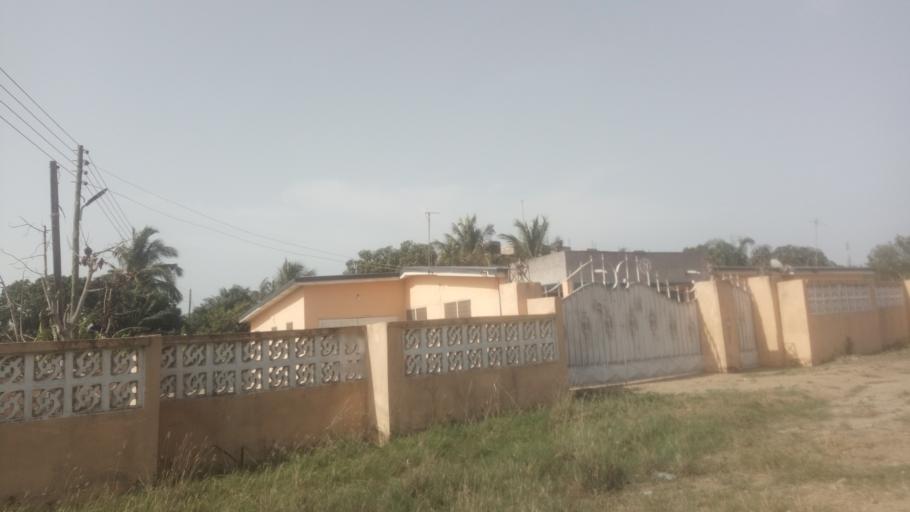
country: GH
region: Central
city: Winneba
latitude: 5.3782
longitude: -0.6483
